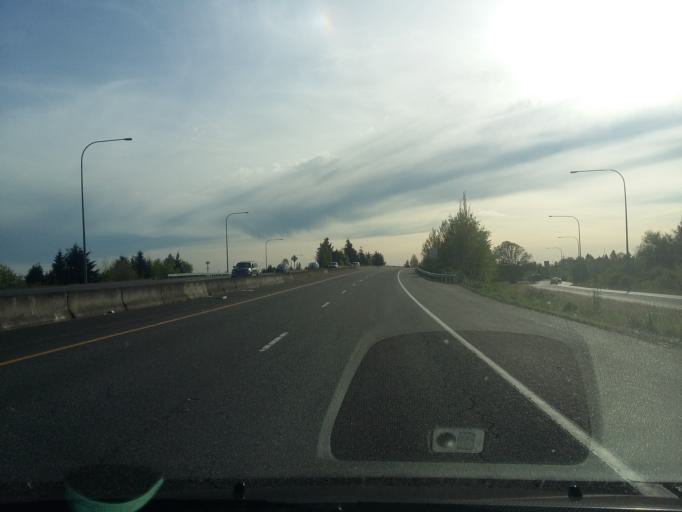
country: US
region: Washington
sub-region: Clark County
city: Walnut Grove
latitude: 45.6501
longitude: -122.5971
